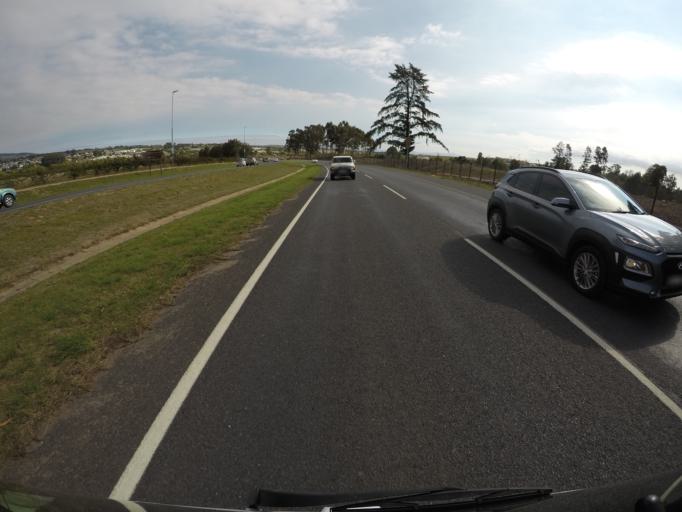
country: ZA
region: Western Cape
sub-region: Cape Winelands District Municipality
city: Stellenbosch
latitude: -33.9653
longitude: 18.8470
